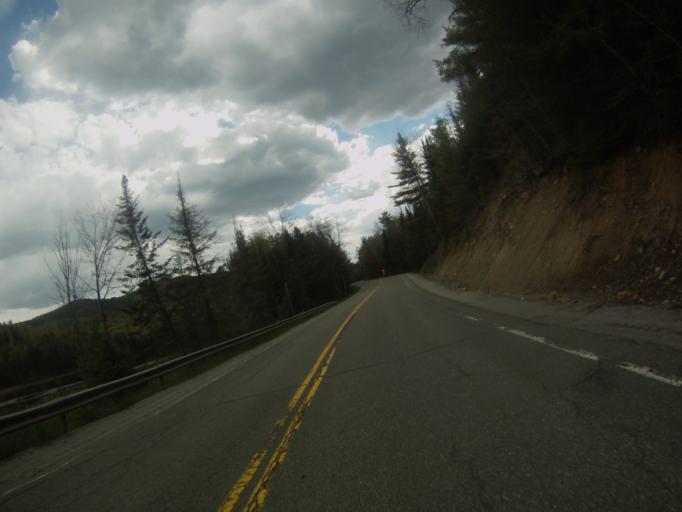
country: US
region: New York
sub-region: Essex County
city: Mineville
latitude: 44.0823
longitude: -73.5925
